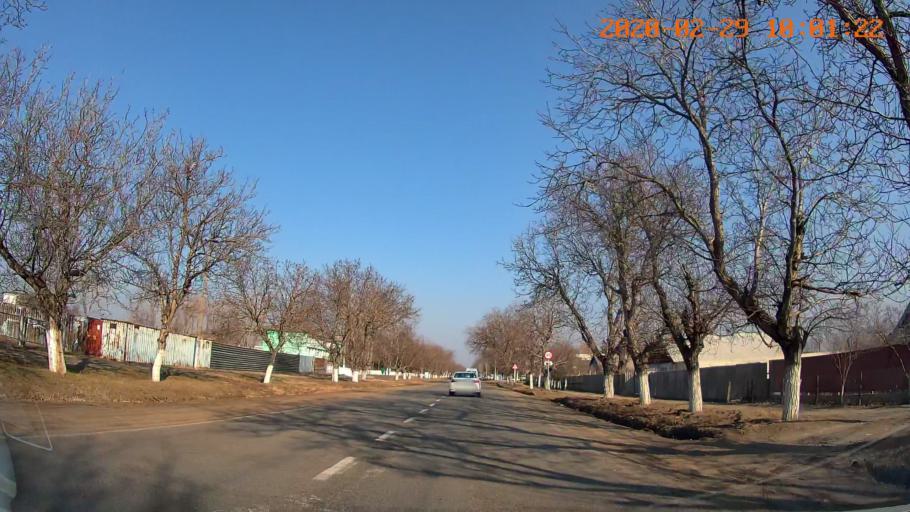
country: MD
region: Telenesti
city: Slobozia
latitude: 46.7748
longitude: 29.6848
